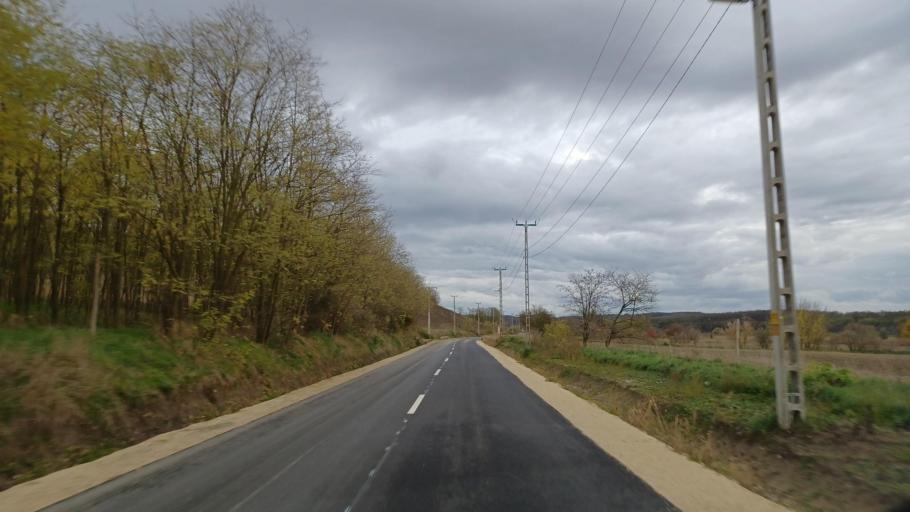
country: HU
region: Tolna
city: Gyonk
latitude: 46.6038
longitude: 18.4240
